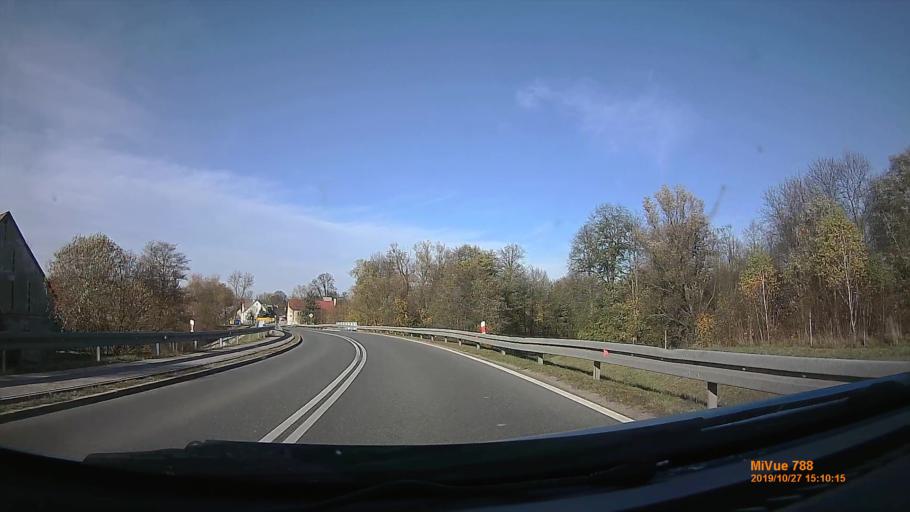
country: PL
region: Lower Silesian Voivodeship
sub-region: Powiat klodzki
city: Miedzylesie
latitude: 50.1865
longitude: 16.6715
